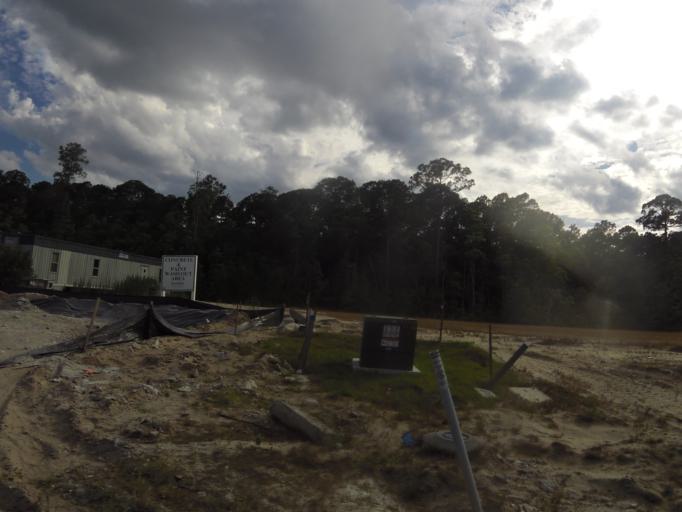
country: US
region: Florida
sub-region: Saint Johns County
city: Palm Valley
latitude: 30.1750
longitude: -81.5107
